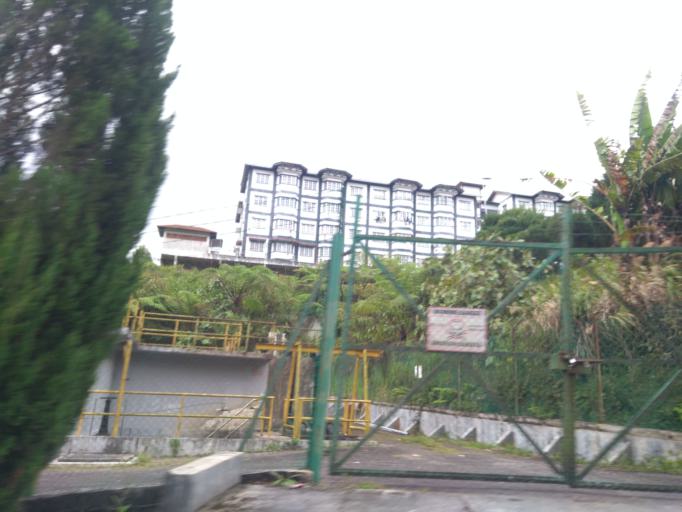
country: MY
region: Pahang
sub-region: Cameron Highlands
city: Tanah Rata
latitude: 4.4685
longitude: 101.3712
